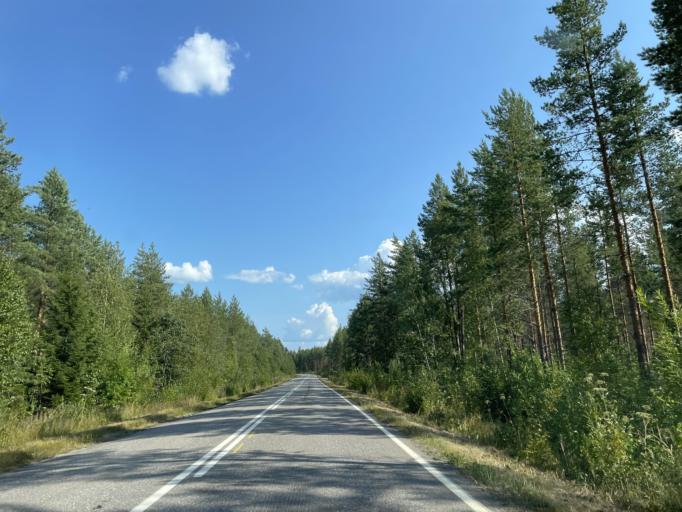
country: FI
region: Central Finland
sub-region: Saarijaervi-Viitasaari
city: Pihtipudas
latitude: 63.3643
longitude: 25.7157
